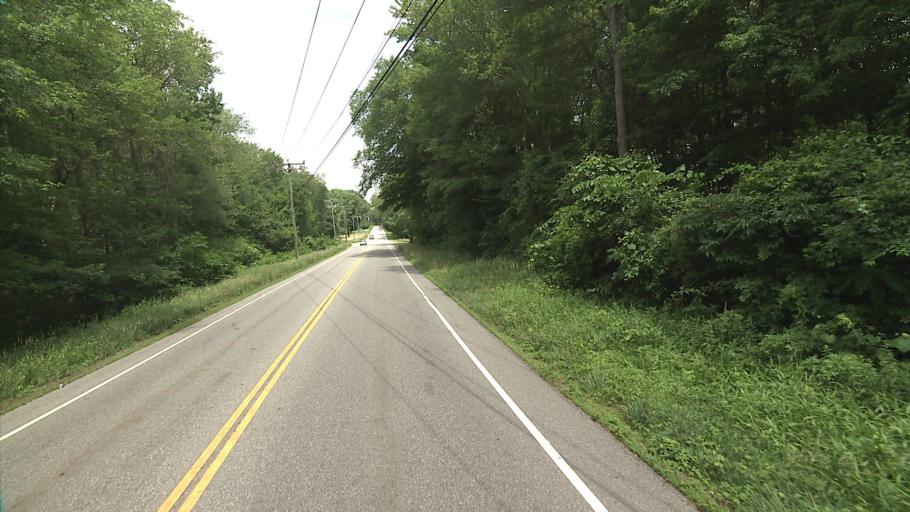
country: US
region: Connecticut
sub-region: New London County
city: Preston City
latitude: 41.5041
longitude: -71.9844
